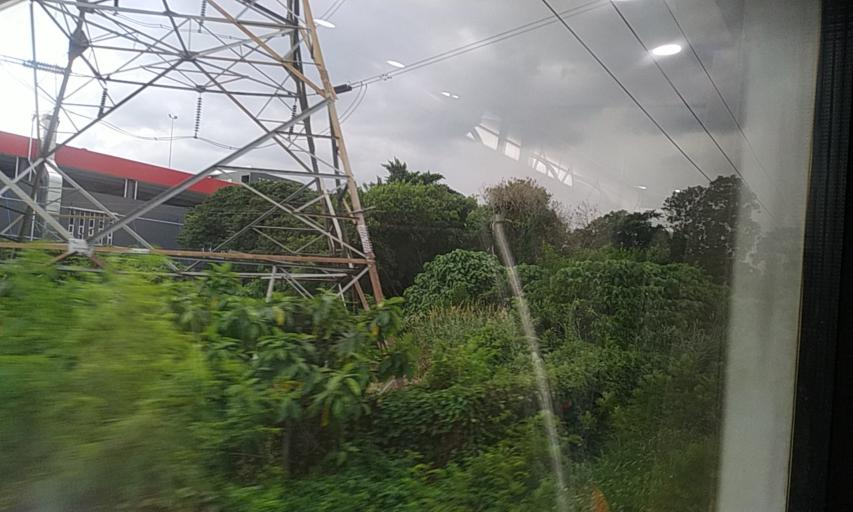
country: MY
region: Kuala Lumpur
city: Kuala Lumpur
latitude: 3.2320
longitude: 101.6765
